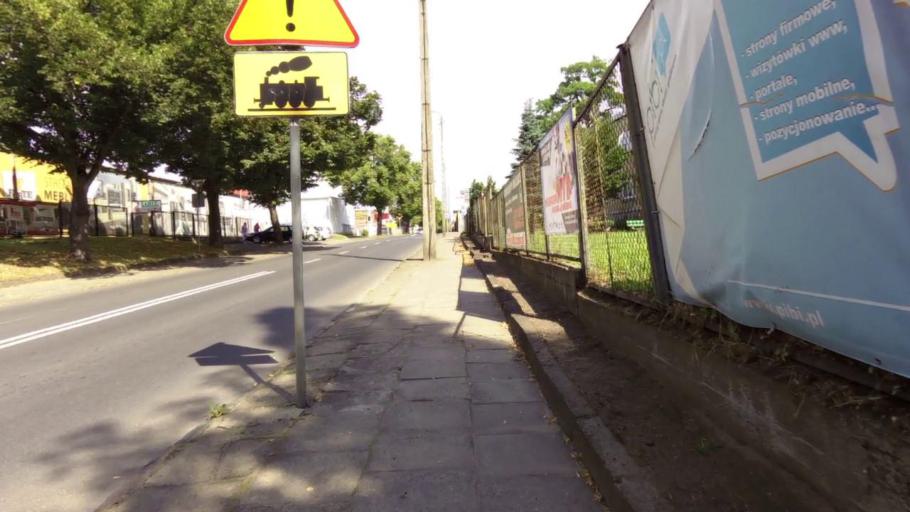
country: PL
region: West Pomeranian Voivodeship
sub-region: Powiat stargardzki
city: Stargard Szczecinski
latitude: 53.3336
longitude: 15.0345
